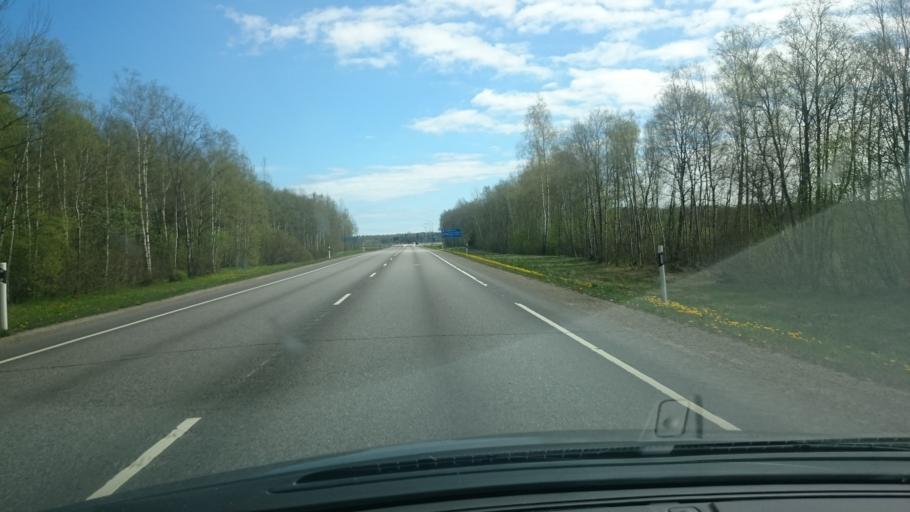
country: EE
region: Ida-Virumaa
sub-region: Kohtla-Jaerve linn
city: Kohtla-Jarve
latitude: 59.4206
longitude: 27.2654
